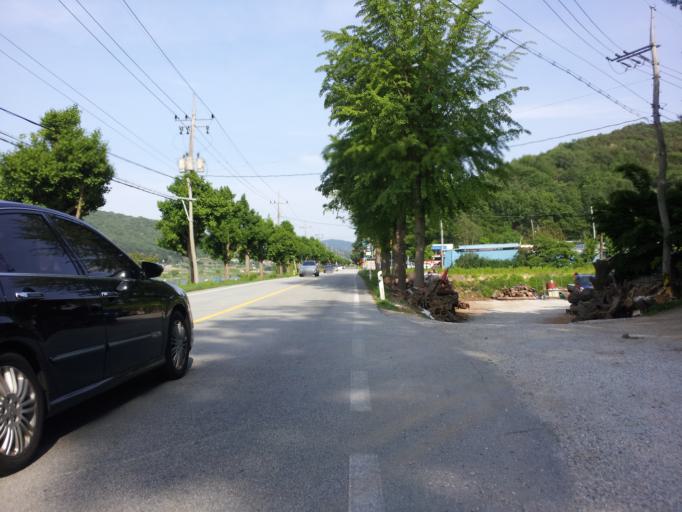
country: KR
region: Chungcheongnam-do
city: Gongju
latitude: 36.4450
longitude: 127.1820
